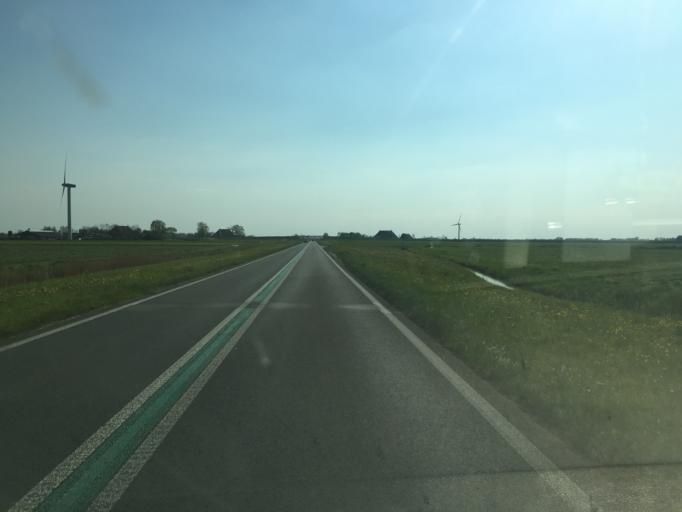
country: NL
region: Friesland
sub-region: Sudwest Fryslan
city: Workum
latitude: 52.9687
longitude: 5.4427
